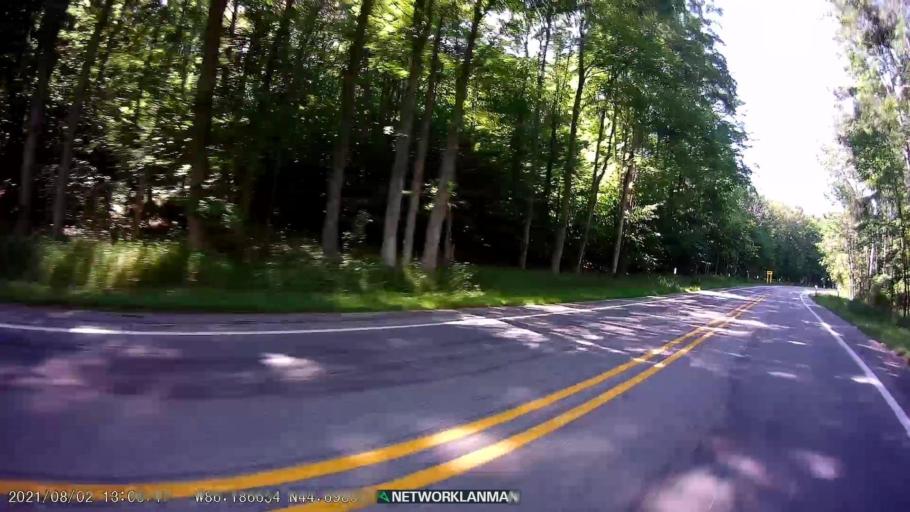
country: US
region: Michigan
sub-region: Benzie County
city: Frankfort
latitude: 44.6973
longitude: -86.1875
